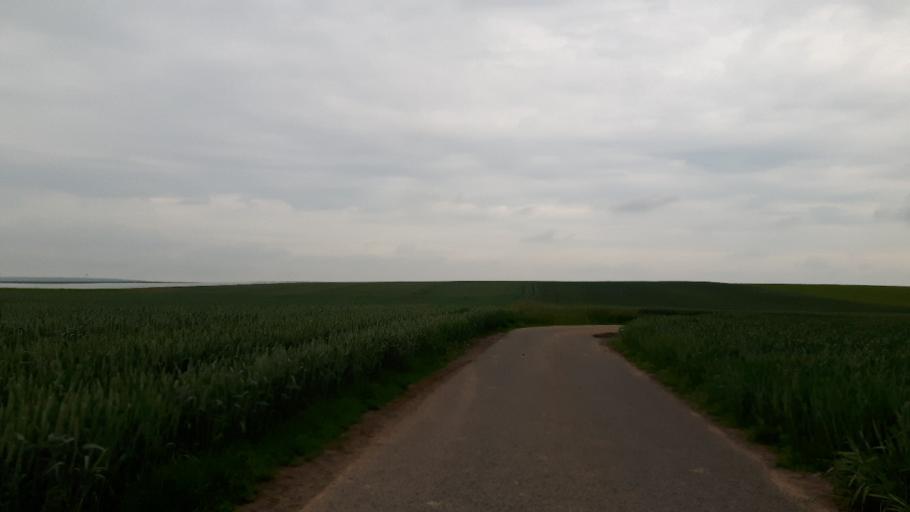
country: DE
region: Bavaria
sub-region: Regierungsbezirk Unterfranken
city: Oberpleichfeld
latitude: 49.8741
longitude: 10.0679
